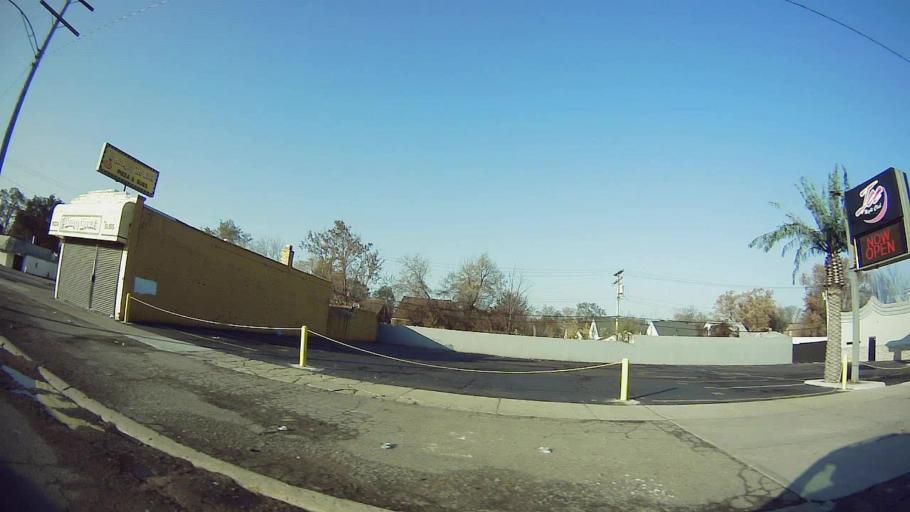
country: US
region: Michigan
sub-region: Wayne County
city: Dearborn
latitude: 42.3695
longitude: -83.1975
